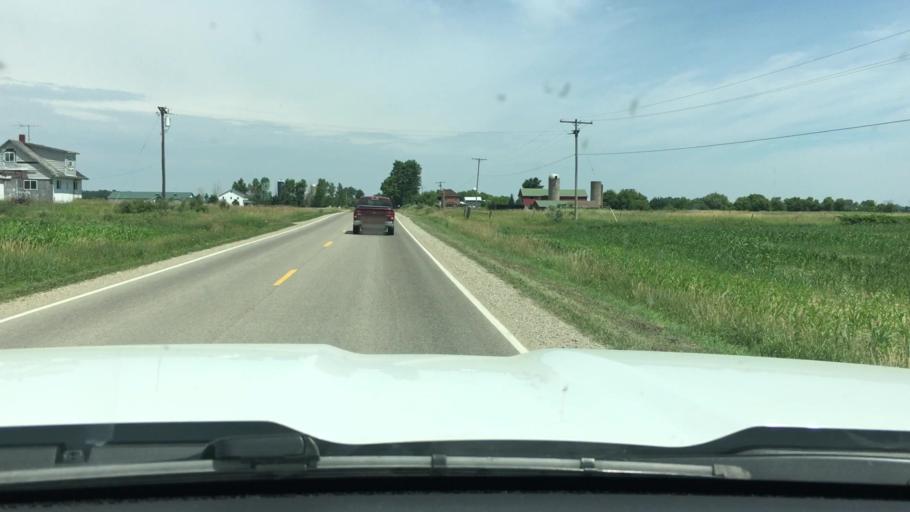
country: US
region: Michigan
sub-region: Sanilac County
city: Brown City
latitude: 43.2683
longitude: -82.9822
